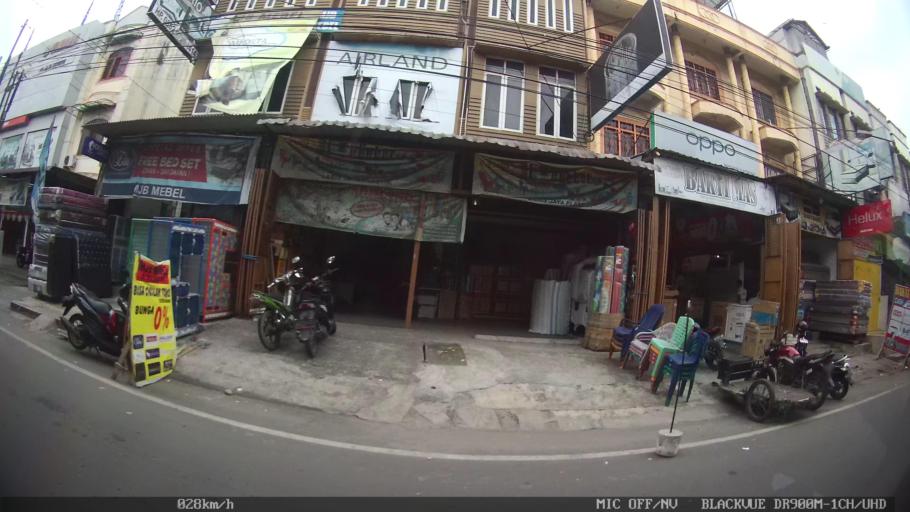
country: ID
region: North Sumatra
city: Medan
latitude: 3.5759
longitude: 98.7029
